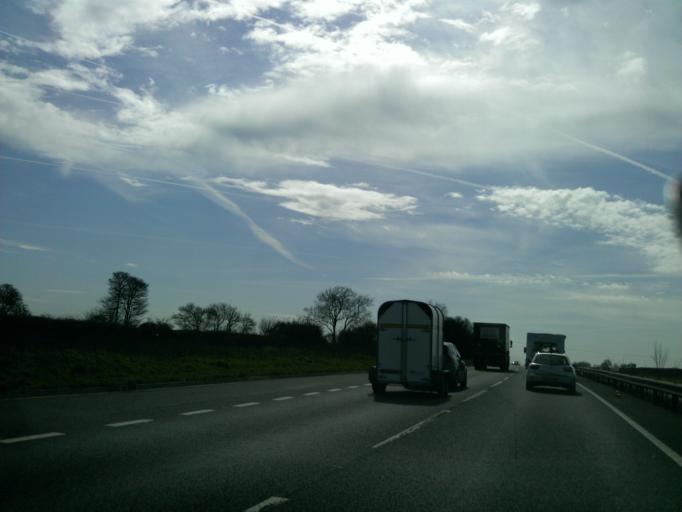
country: GB
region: England
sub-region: Essex
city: Marks Tey
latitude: 51.8609
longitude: 0.7490
